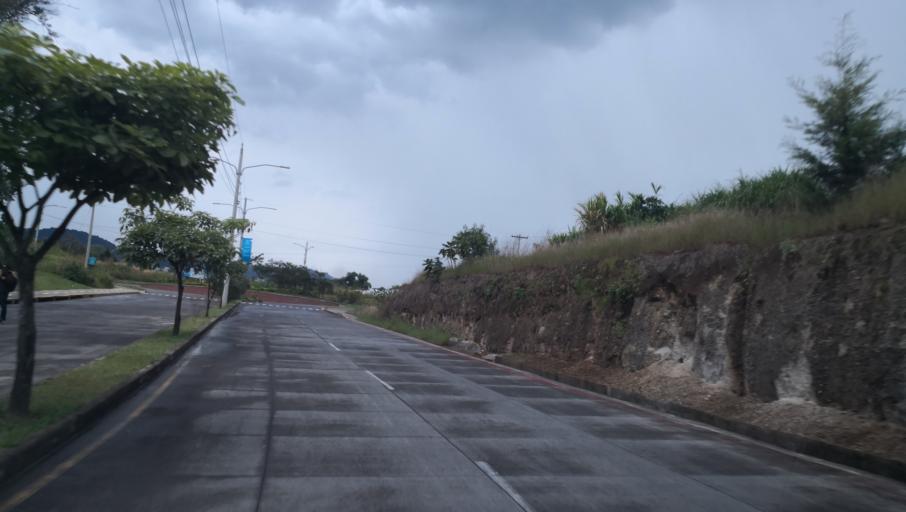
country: GT
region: Guatemala
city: Villa Nueva
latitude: 14.5576
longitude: -90.5949
